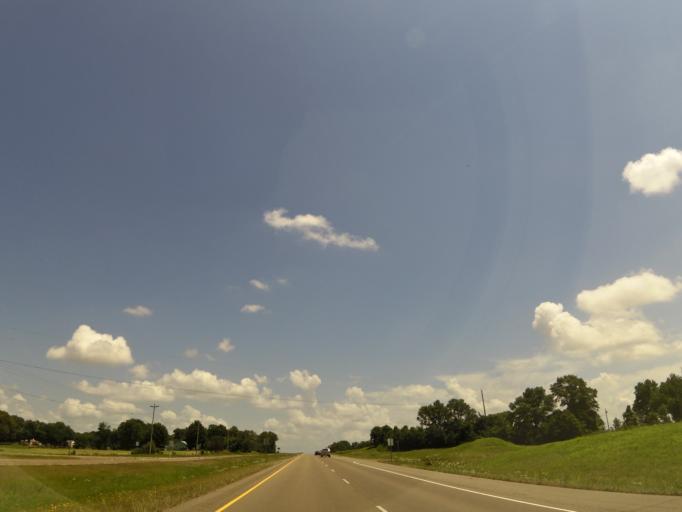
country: US
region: Tennessee
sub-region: Crockett County
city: Alamo
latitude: 35.8354
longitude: -89.1846
